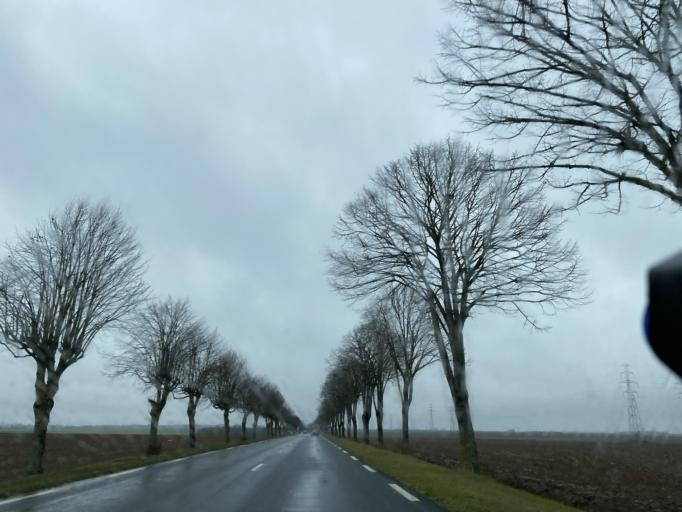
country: FR
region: Centre
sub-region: Departement d'Eure-et-Loir
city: Baigneaux
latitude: 48.1691
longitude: 1.8378
